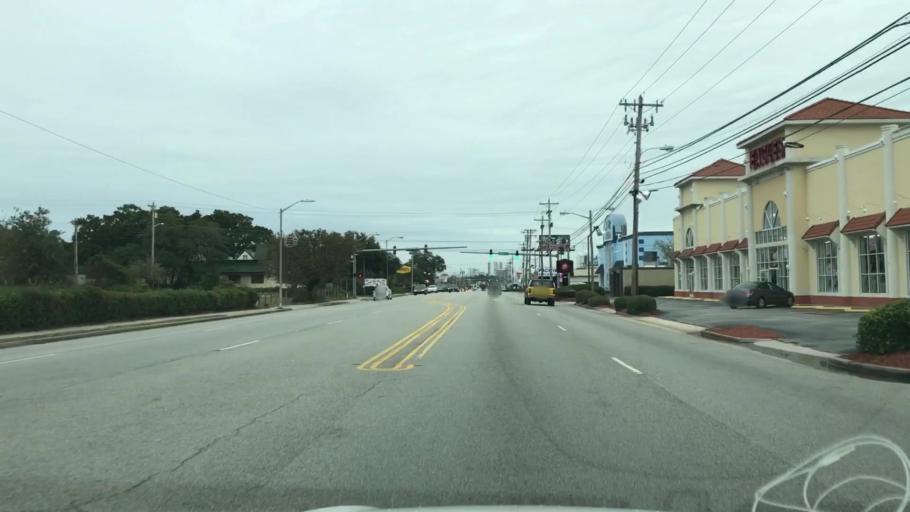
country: US
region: South Carolina
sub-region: Horry County
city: Myrtle Beach
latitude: 33.6793
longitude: -78.8989
